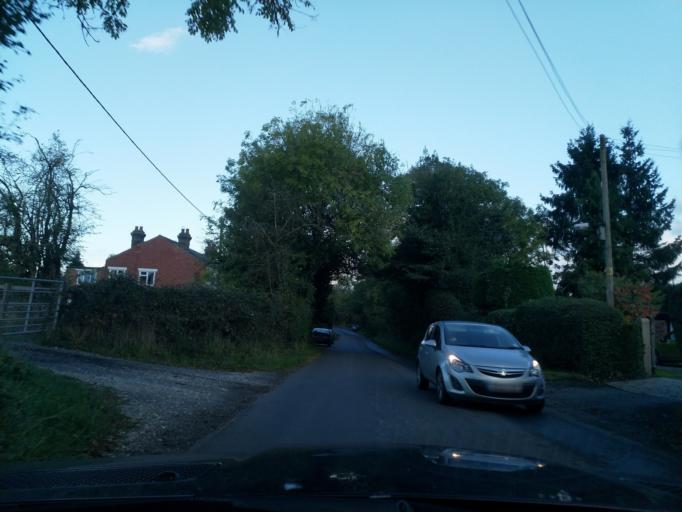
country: GB
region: England
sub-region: Solihull
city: Knowle
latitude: 52.3480
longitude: -1.7200
